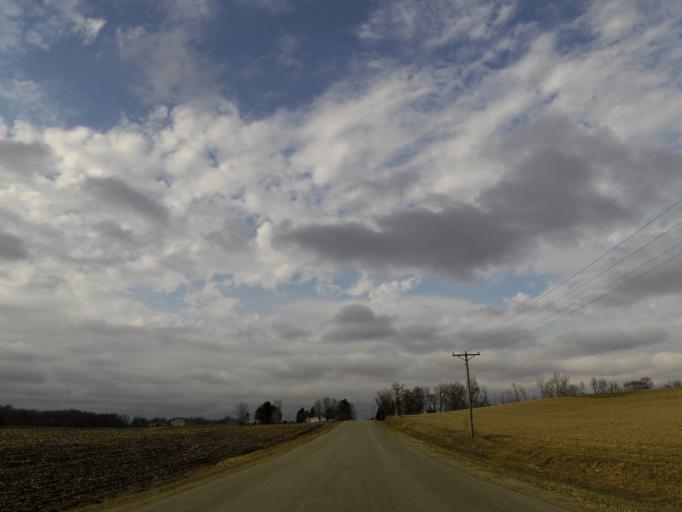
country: US
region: Wisconsin
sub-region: Pierce County
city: Ellsworth
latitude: 44.7479
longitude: -92.4668
